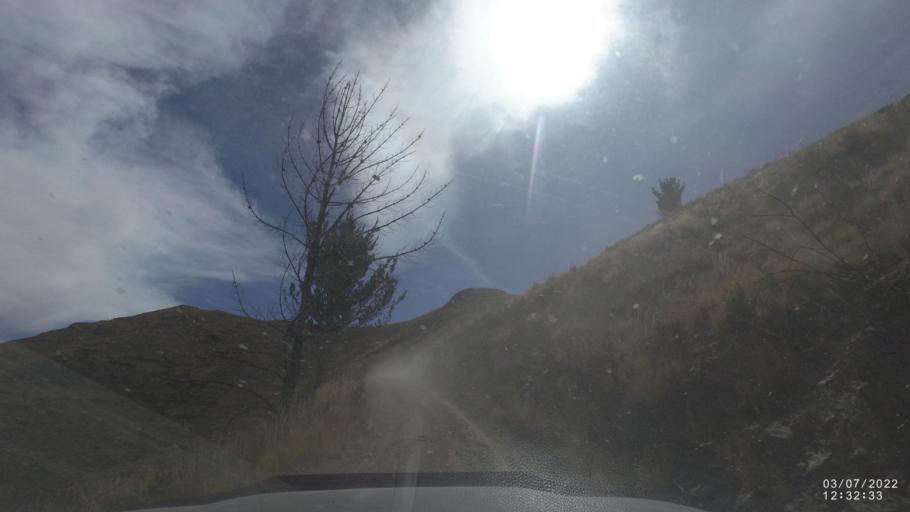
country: BO
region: Cochabamba
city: Irpa Irpa
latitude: -17.8091
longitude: -66.6058
